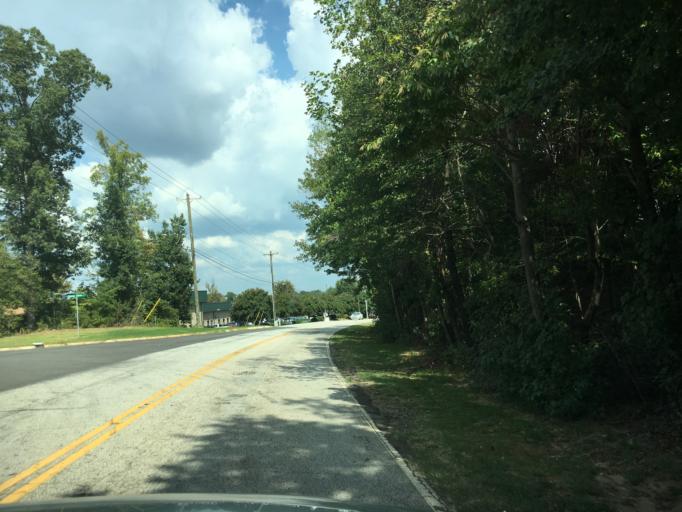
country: US
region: South Carolina
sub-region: Greenville County
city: Mauldin
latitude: 34.8336
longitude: -82.2912
